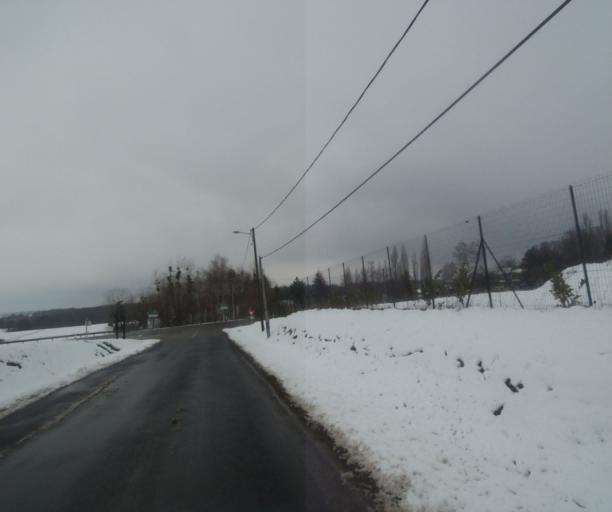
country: FR
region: Champagne-Ardenne
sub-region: Departement de la Haute-Marne
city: Montier-en-Der
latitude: 48.5185
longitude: 4.8103
